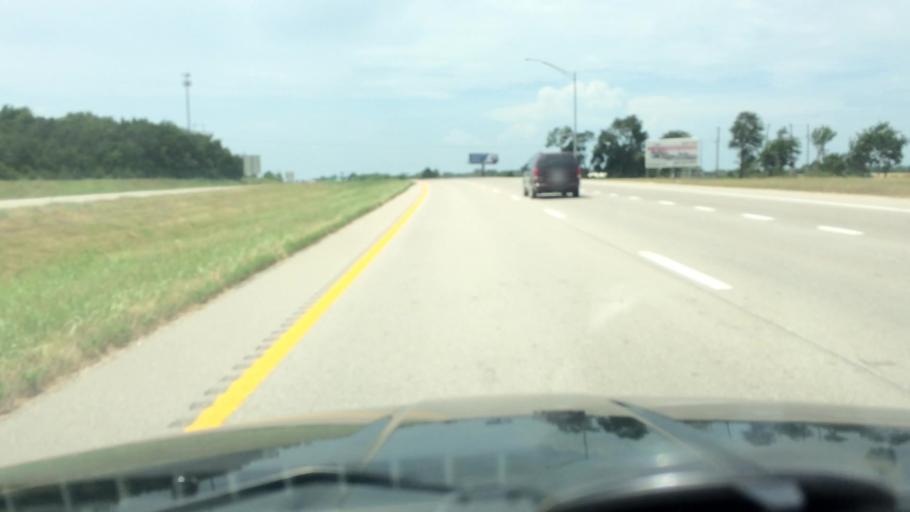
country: US
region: Missouri
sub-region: Polk County
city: Bolivar
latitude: 37.5777
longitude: -93.4014
